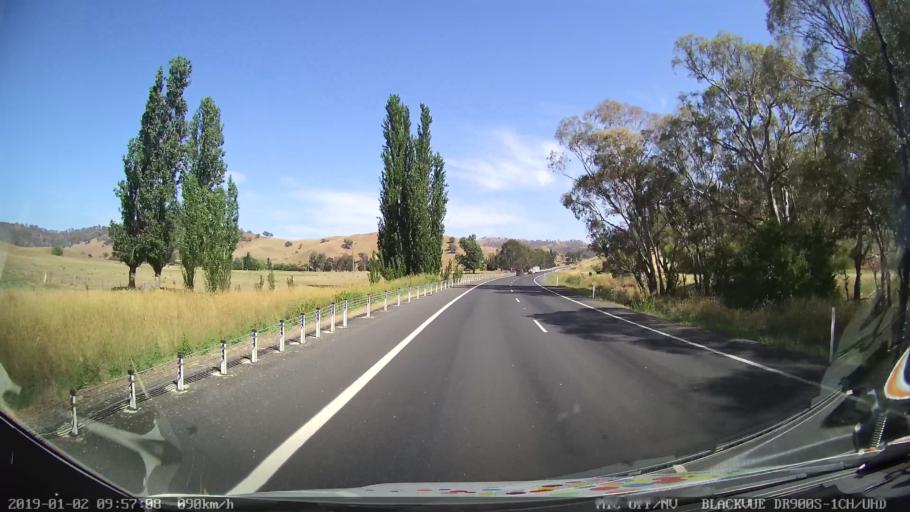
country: AU
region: New South Wales
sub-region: Tumut Shire
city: Tumut
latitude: -35.2091
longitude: 148.1684
